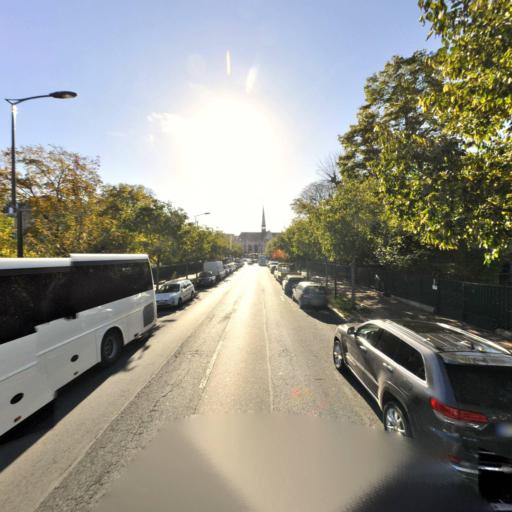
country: FR
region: Ile-de-France
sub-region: Departement des Hauts-de-Seine
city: Boulogne-Billancourt
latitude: 48.8477
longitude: 2.2370
